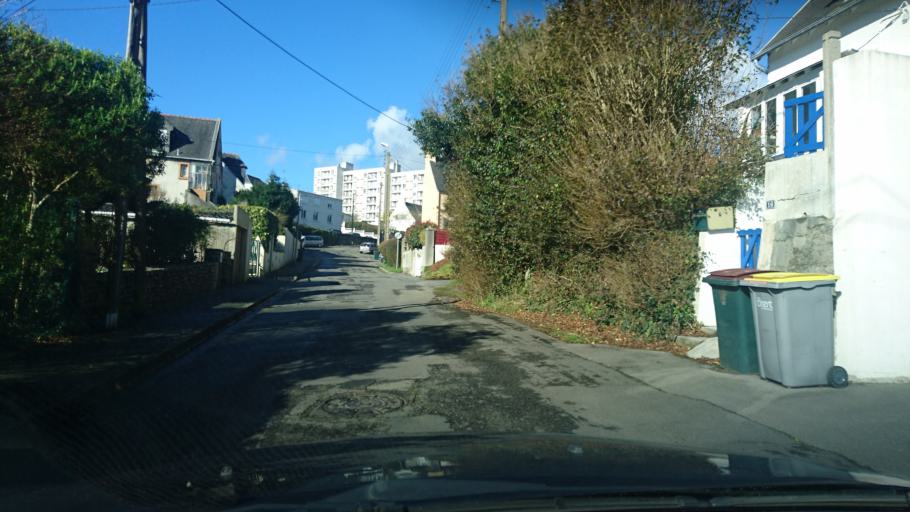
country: FR
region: Brittany
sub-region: Departement du Finistere
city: Brest
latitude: 48.3952
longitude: -4.4565
